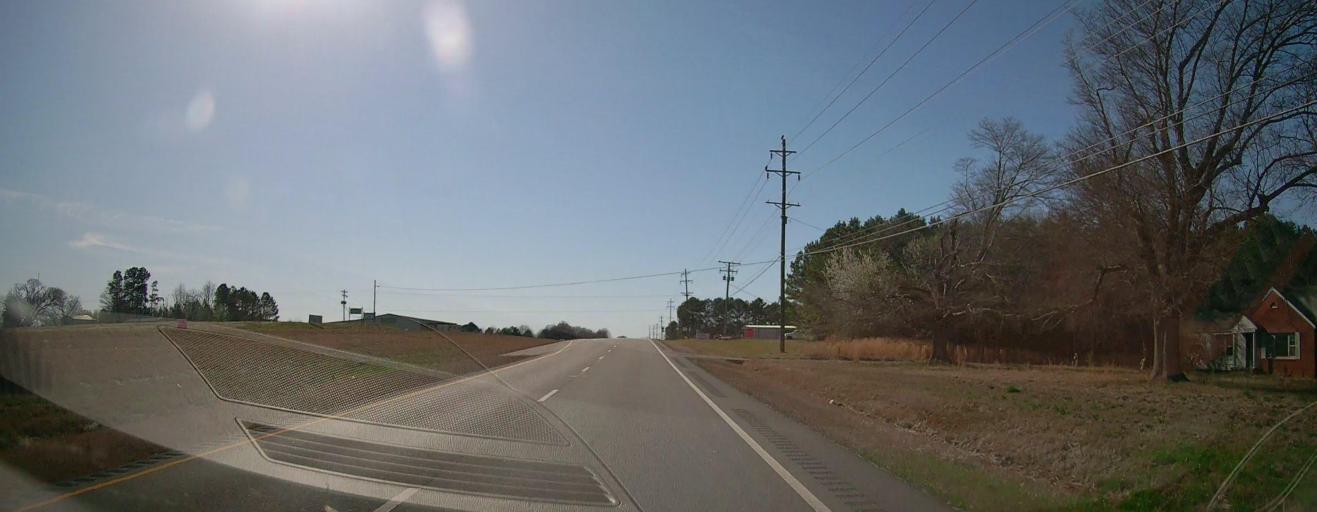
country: US
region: Alabama
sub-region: Lauderdale County
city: Killen
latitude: 34.8601
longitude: -87.4323
